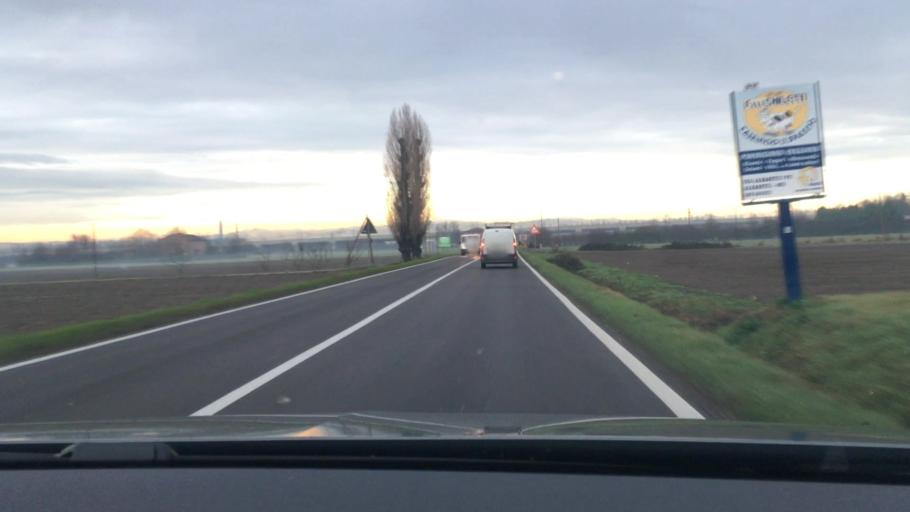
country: IT
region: Emilia-Romagna
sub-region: Provincia di Modena
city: Albareto
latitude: 44.6969
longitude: 10.9471
